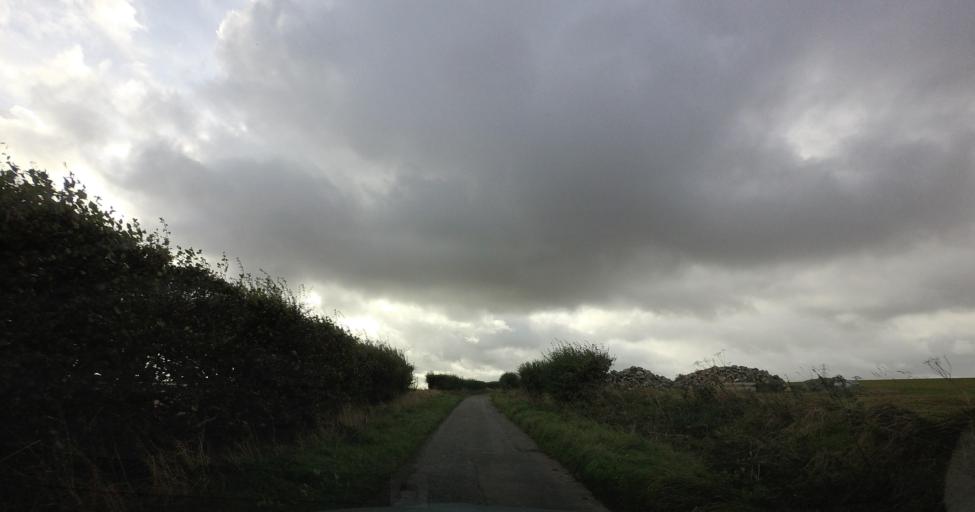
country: GB
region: Scotland
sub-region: Aberdeenshire
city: Whitehills
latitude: 57.6599
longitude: -2.6091
